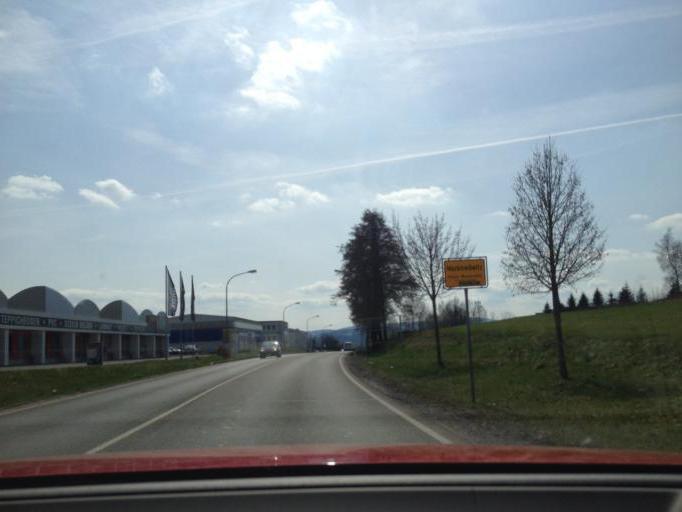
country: DE
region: Bavaria
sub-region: Upper Franconia
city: Marktredwitz
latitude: 50.0099
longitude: 12.0775
